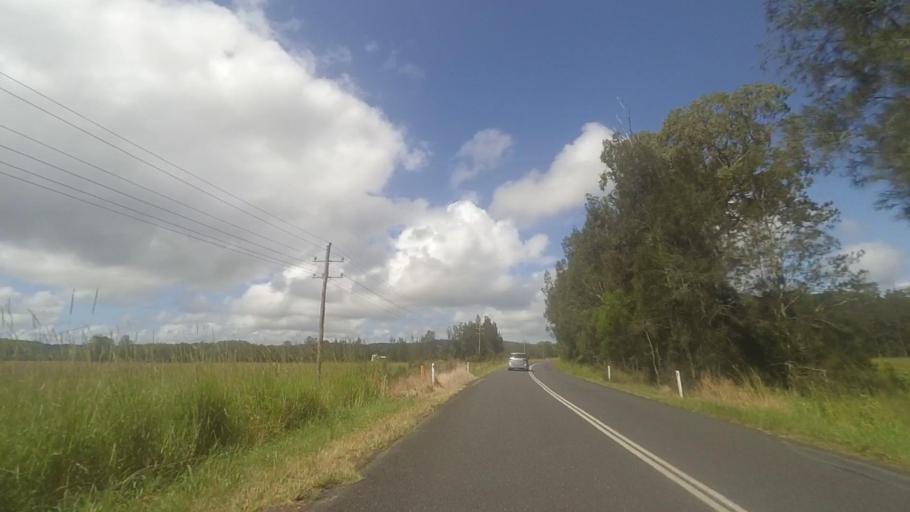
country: AU
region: New South Wales
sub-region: Great Lakes
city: Bulahdelah
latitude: -32.3916
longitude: 152.3278
